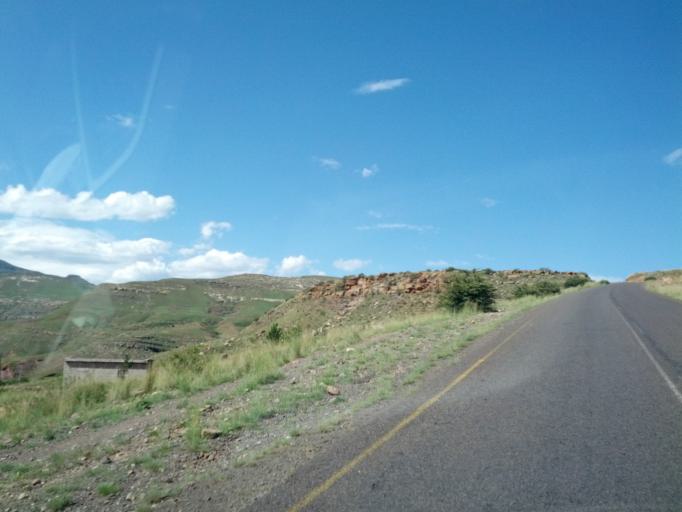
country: LS
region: Qacha's Nek
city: Qacha's Nek
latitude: -30.0544
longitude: 28.4836
